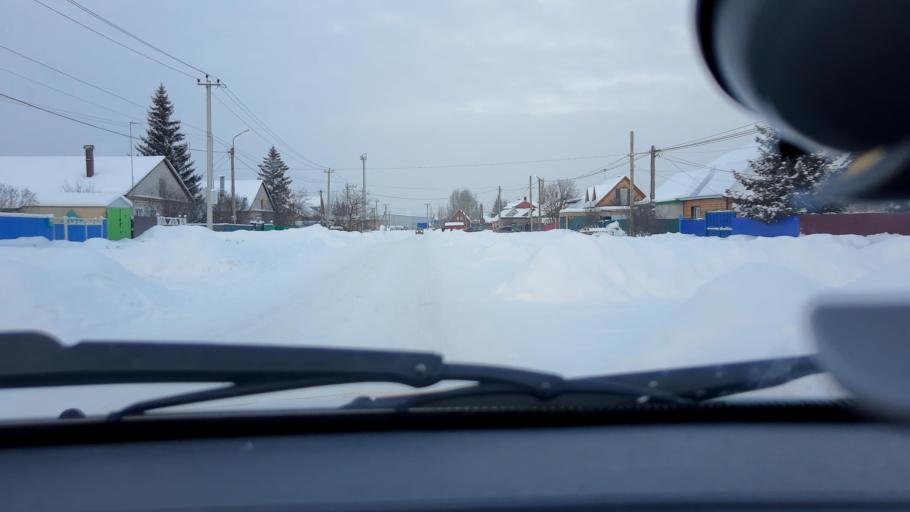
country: RU
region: Bashkortostan
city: Ufa
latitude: 54.6128
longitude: 55.8980
